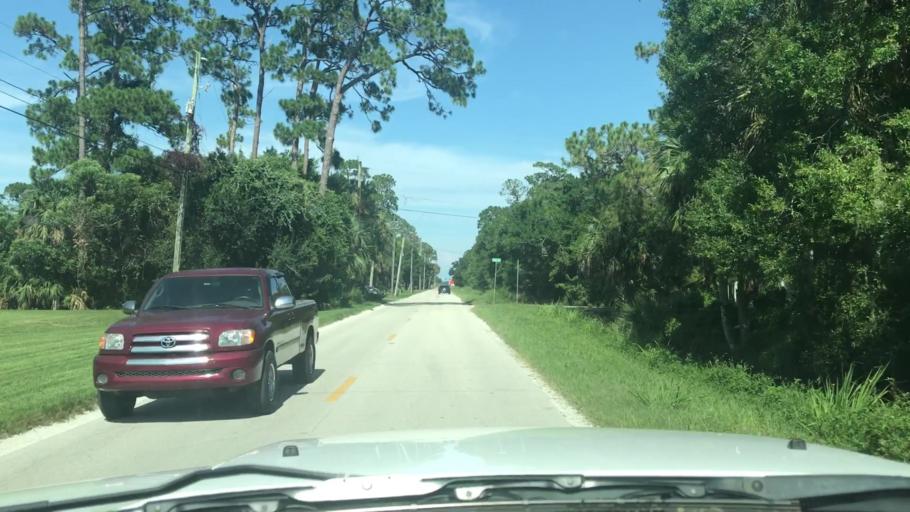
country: US
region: Florida
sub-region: Indian River County
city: Gifford
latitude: 27.6680
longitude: -80.4529
